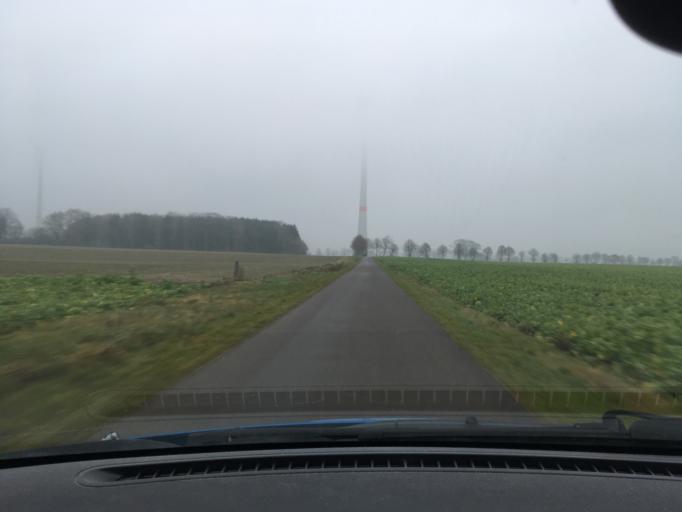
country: DE
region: Lower Saxony
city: Amelinghausen
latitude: 53.1067
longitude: 10.1930
